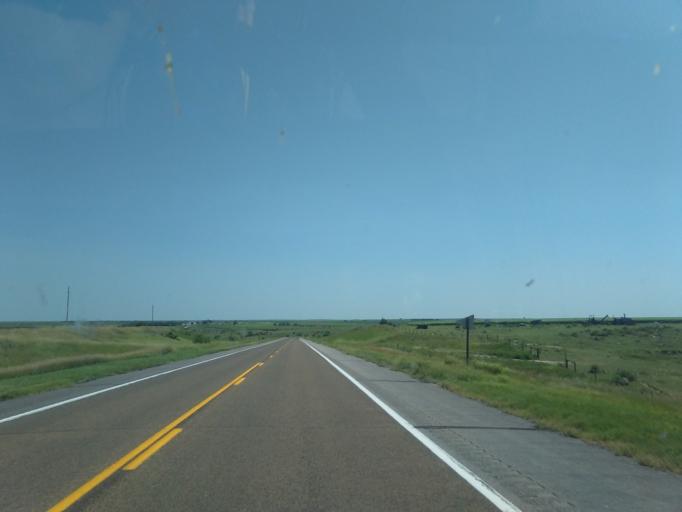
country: US
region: Nebraska
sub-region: Hitchcock County
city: Trenton
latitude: 40.1717
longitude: -101.1464
